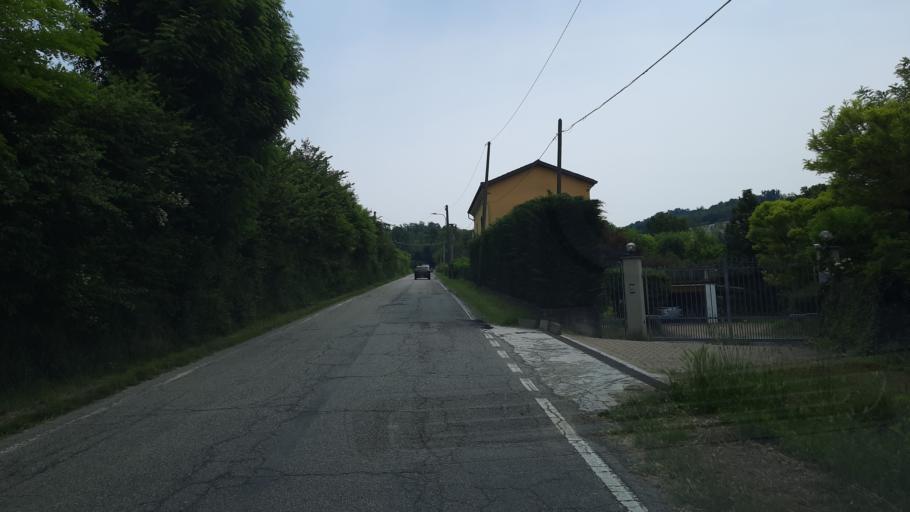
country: IT
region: Piedmont
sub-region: Provincia di Alessandria
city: Ozzano Monferrato
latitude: 45.1015
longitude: 8.3830
